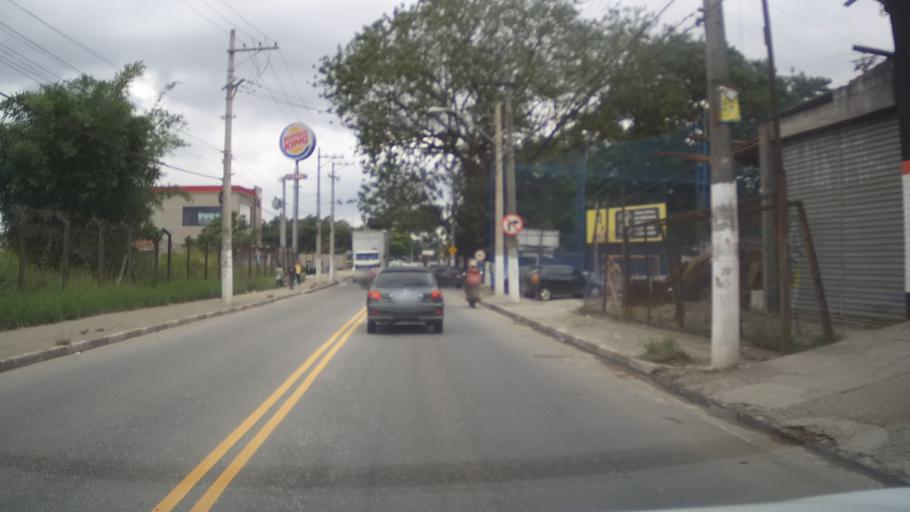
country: BR
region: Sao Paulo
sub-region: Itaquaquecetuba
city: Itaquaquecetuba
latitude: -23.4519
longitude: -46.4072
